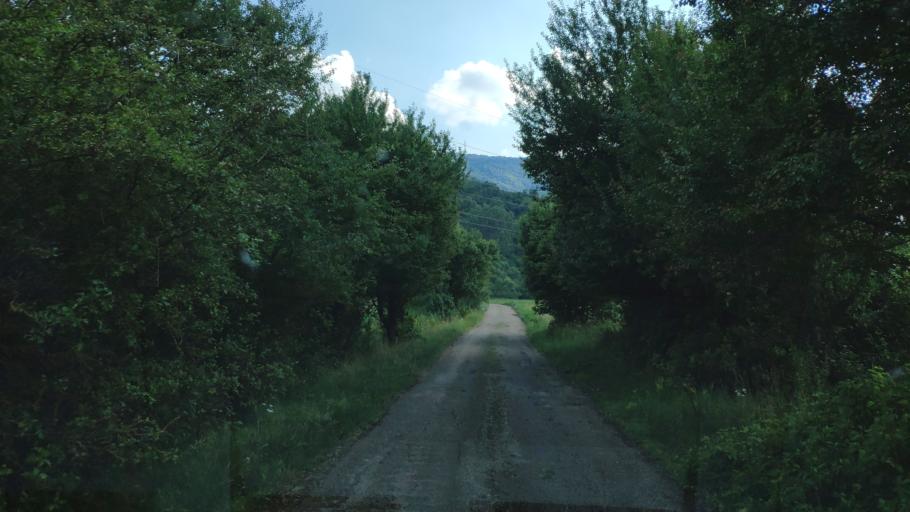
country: HU
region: Borsod-Abauj-Zemplen
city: Szendro
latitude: 48.5922
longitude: 20.7283
